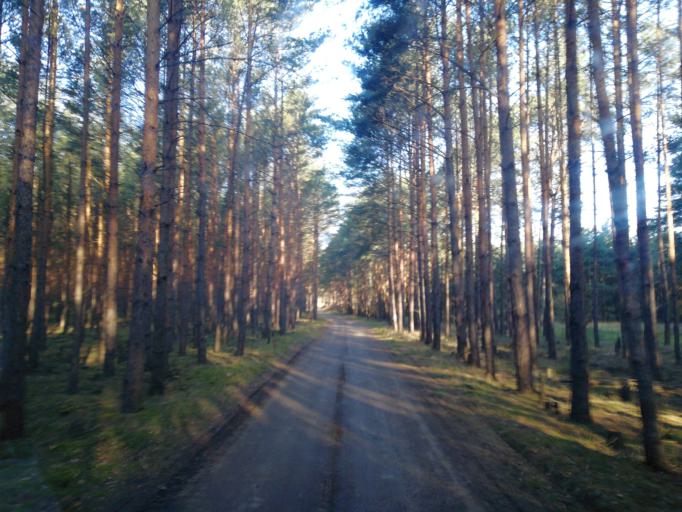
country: DE
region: Brandenburg
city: Drahnsdorf
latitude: 51.9447
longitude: 13.5681
